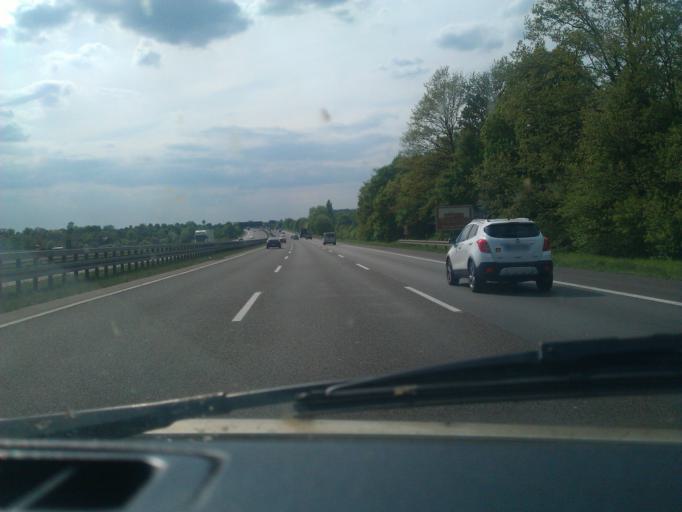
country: DE
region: North Rhine-Westphalia
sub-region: Regierungsbezirk Dusseldorf
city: Moers
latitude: 51.4946
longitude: 6.6239
